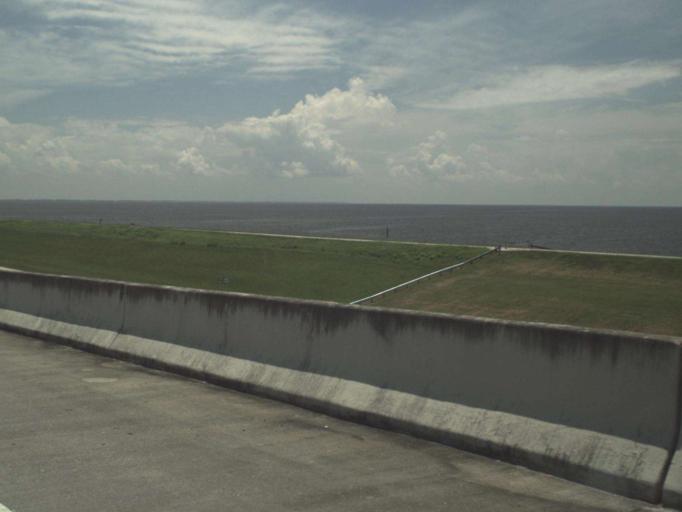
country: US
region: Florida
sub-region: Martin County
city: Indiantown
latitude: 26.9823
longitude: -80.6162
